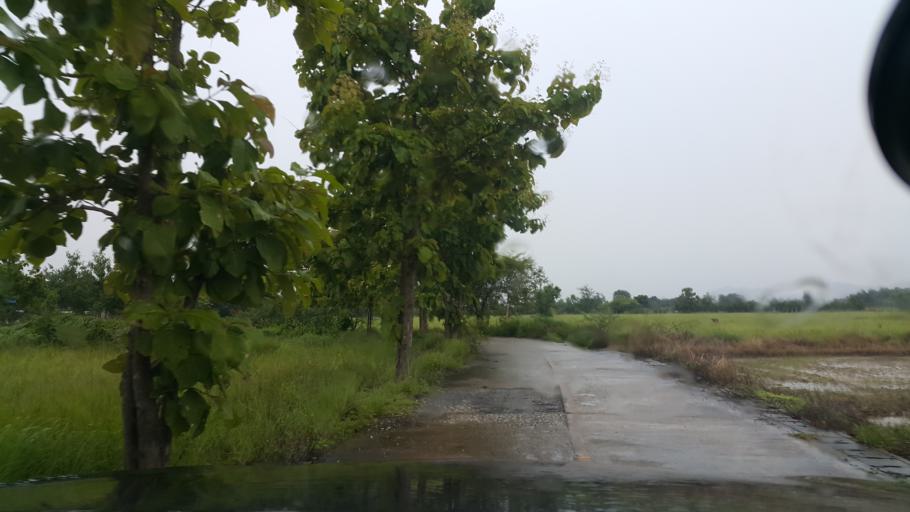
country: TH
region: Lamphun
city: Ban Thi
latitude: 18.6258
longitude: 99.1150
